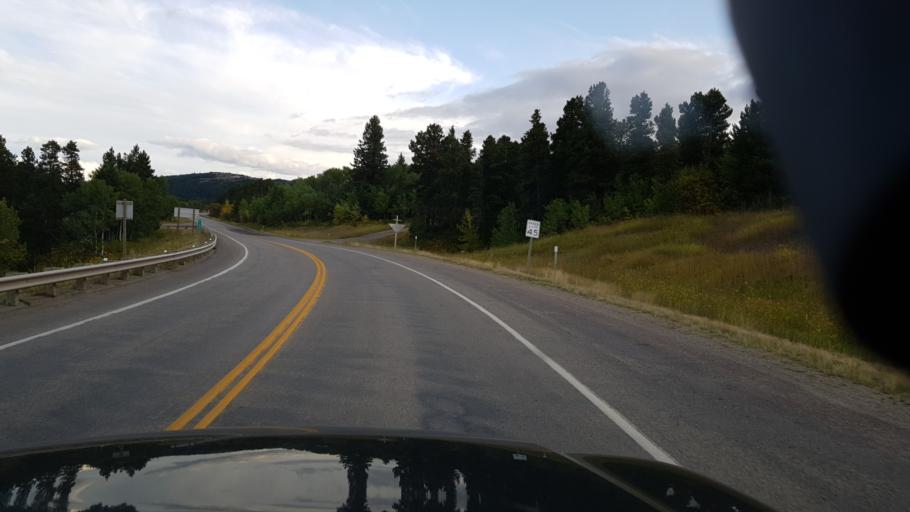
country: US
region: Montana
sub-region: Glacier County
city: South Browning
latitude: 48.4384
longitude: -113.2188
